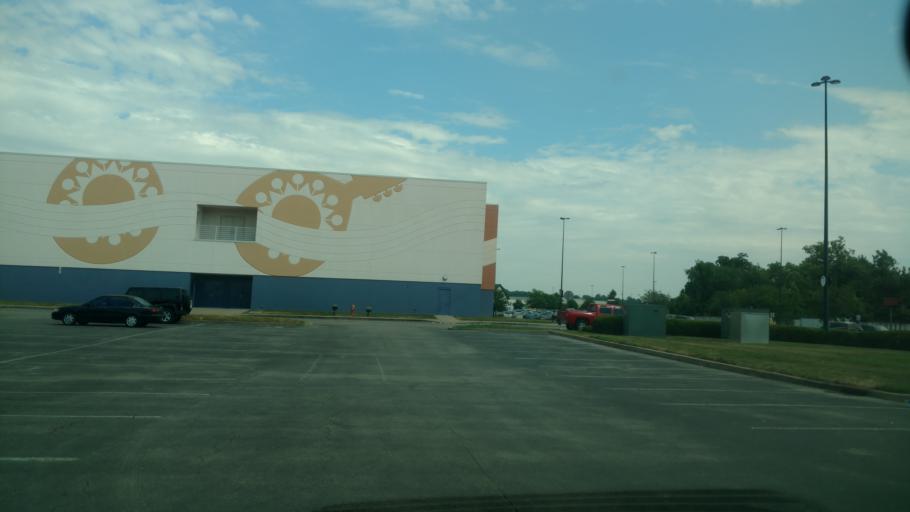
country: US
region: Tennessee
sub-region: Davidson County
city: Lakewood
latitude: 36.2062
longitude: -86.6966
